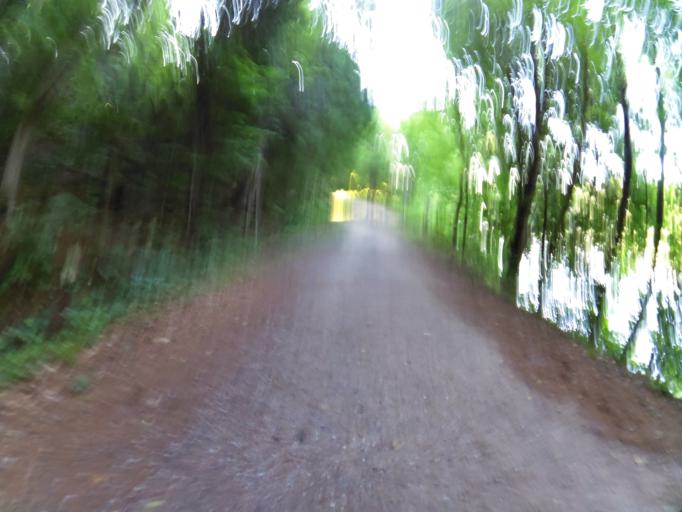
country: CA
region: Quebec
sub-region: Outaouais
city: Wakefield
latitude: 45.5982
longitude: -75.9961
